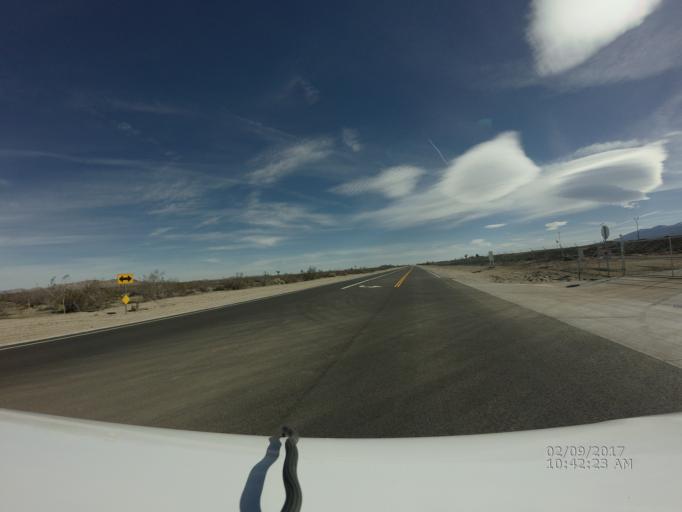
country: US
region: California
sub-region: Los Angeles County
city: Littlerock
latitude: 34.5427
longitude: -117.8963
